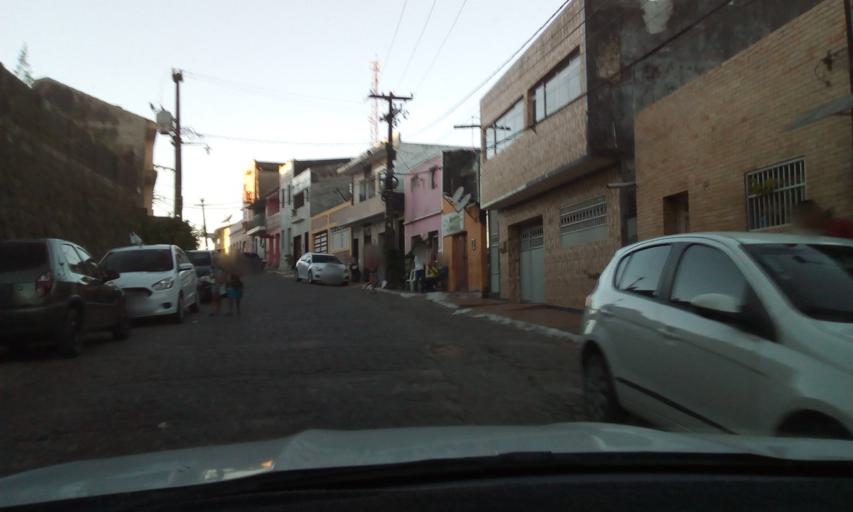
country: BR
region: Paraiba
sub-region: Areia
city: Areia
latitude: -6.9704
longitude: -35.7040
